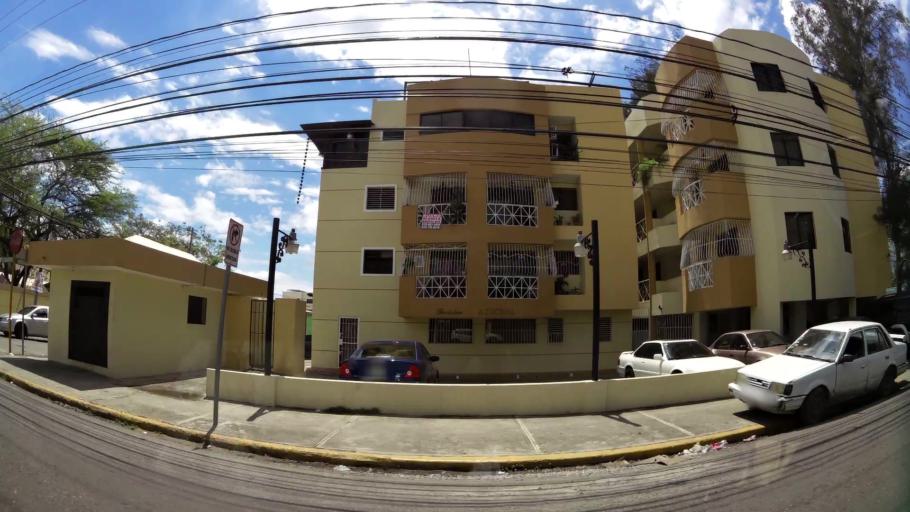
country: DO
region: Santiago
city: Santiago de los Caballeros
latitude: 19.4598
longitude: -70.6624
